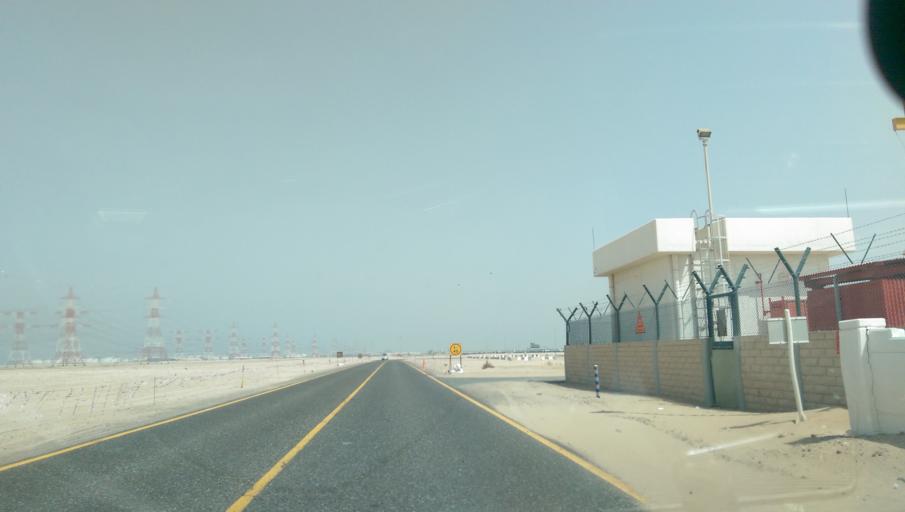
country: AE
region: Abu Dhabi
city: Abu Dhabi
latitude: 24.2968
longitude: 54.5398
